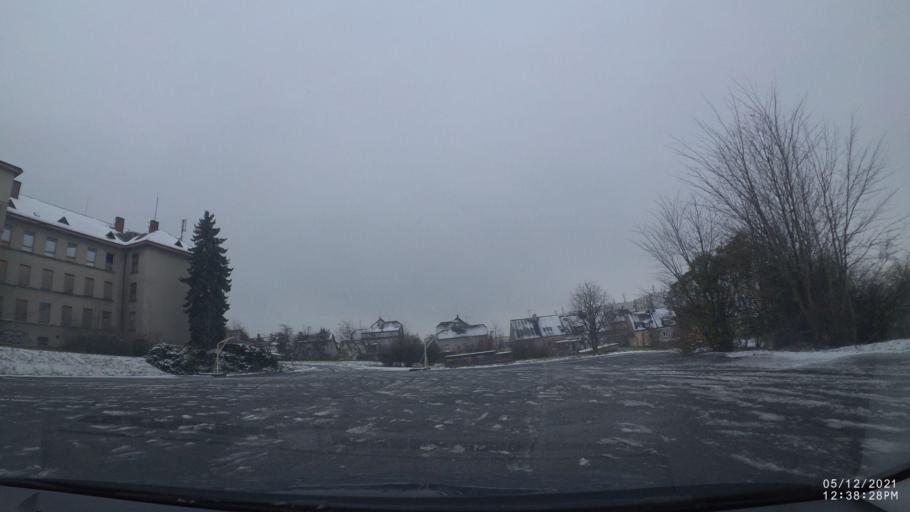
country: CZ
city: Nove Mesto nad Metuji
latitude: 50.3547
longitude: 16.1515
